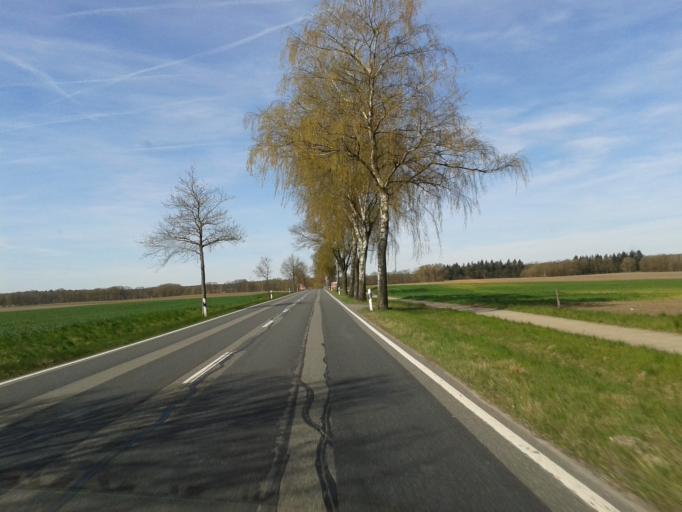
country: DE
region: Lower Saxony
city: Eimke
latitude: 52.9666
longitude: 10.3394
